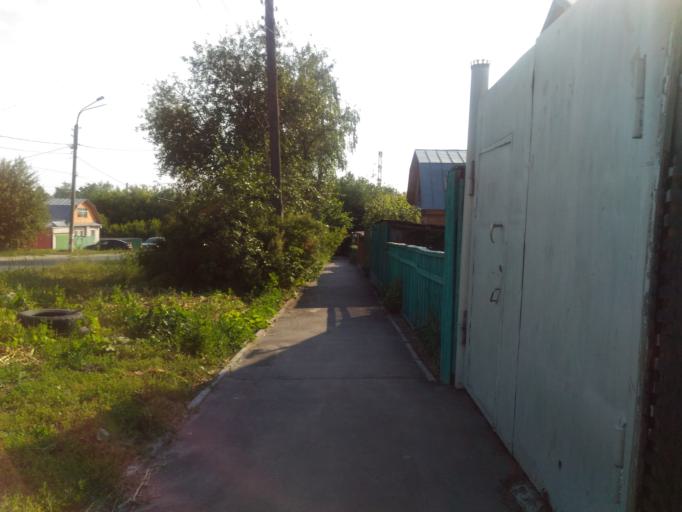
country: RU
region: Ulyanovsk
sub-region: Ulyanovskiy Rayon
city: Ulyanovsk
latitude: 54.3386
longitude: 48.3618
